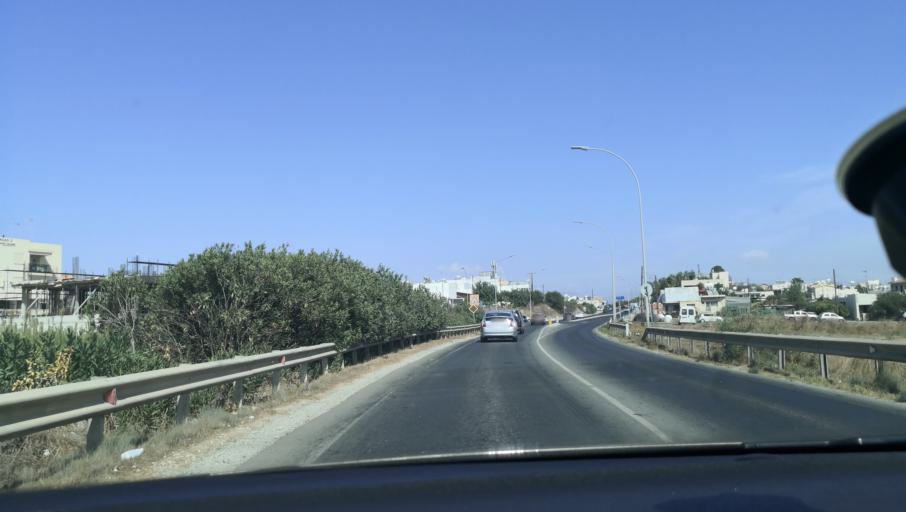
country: CY
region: Lefkosia
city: Kato Deftera
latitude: 35.1133
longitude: 33.2845
